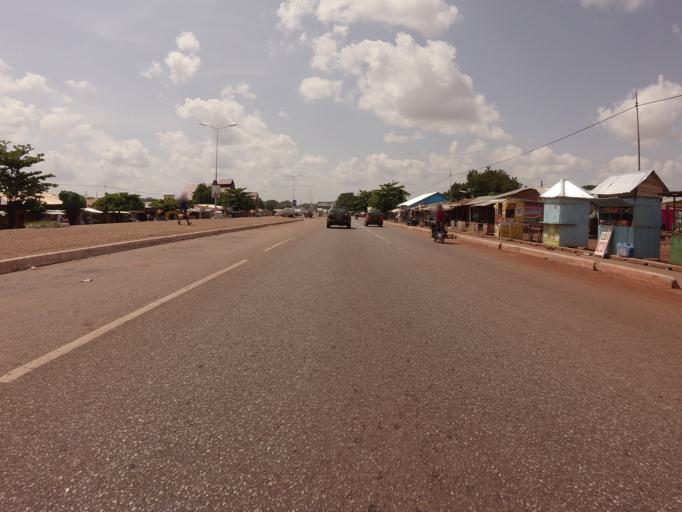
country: GH
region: Northern
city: Tamale
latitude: 9.4189
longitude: -0.8417
